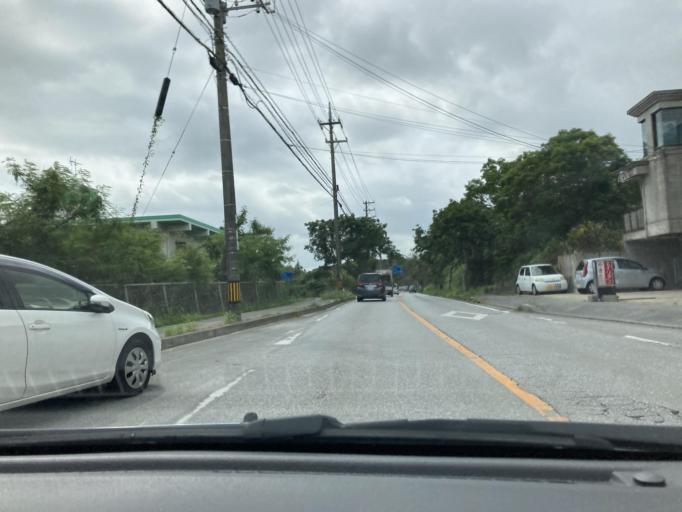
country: JP
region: Okinawa
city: Ginowan
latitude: 26.2776
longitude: 127.7829
